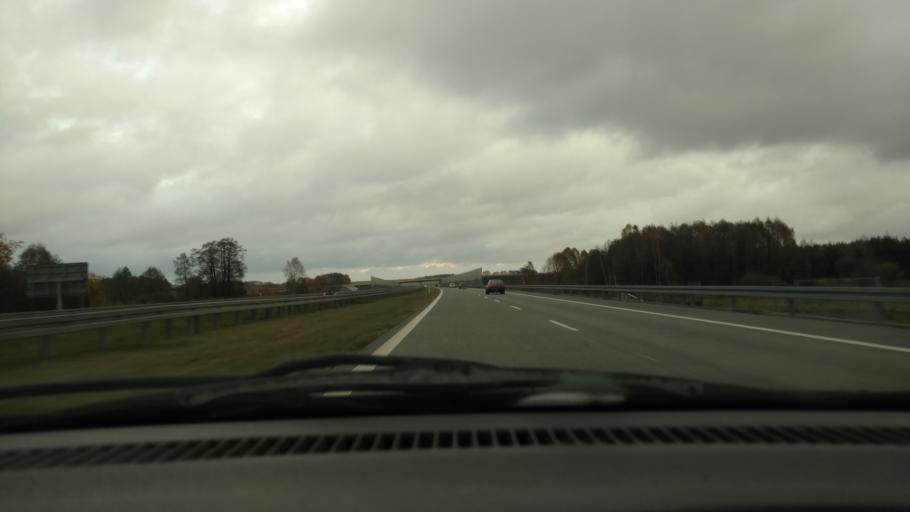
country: PL
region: Lodz Voivodeship
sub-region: Powiat pabianicki
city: Pabianice
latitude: 51.6180
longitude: 19.3770
